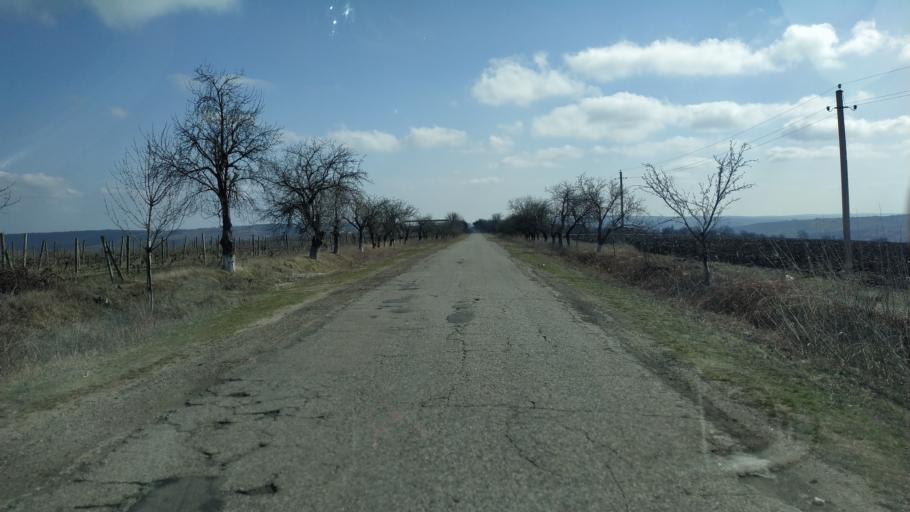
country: MD
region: Hincesti
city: Hincesti
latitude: 46.8499
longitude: 28.6499
